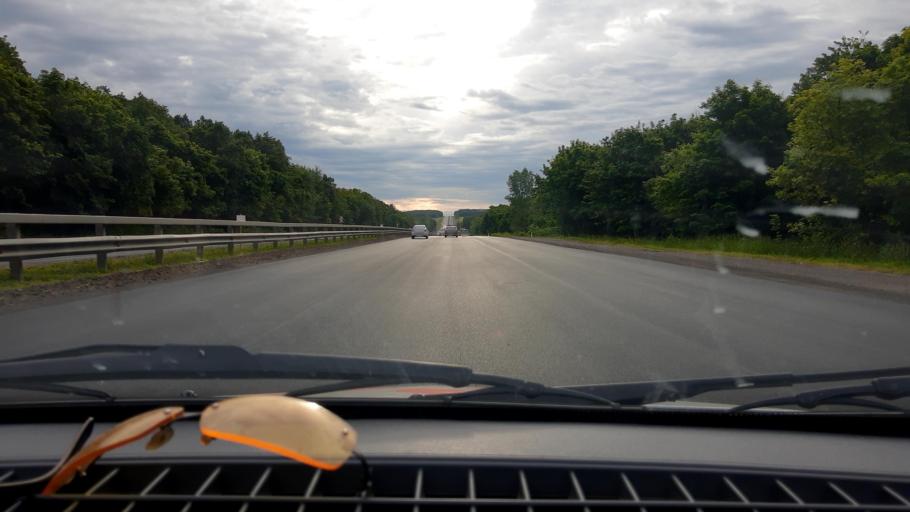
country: RU
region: Bashkortostan
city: Avdon
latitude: 54.6448
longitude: 55.6317
